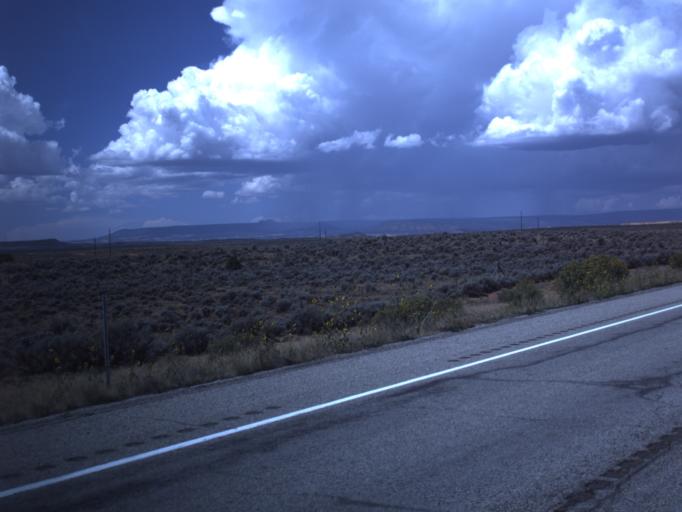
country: US
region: Utah
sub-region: San Juan County
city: Blanding
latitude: 37.5109
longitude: -109.4920
